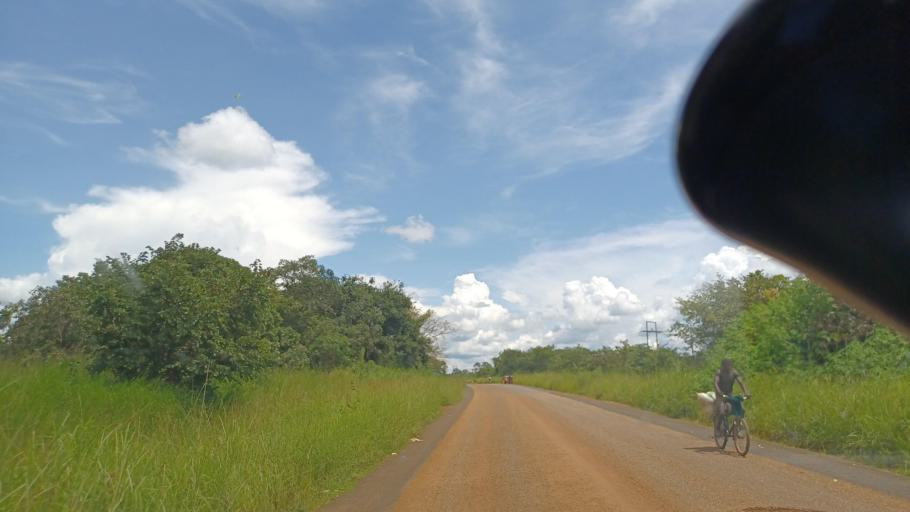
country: ZM
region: North-Western
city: Solwezi
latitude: -12.5587
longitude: 26.1428
